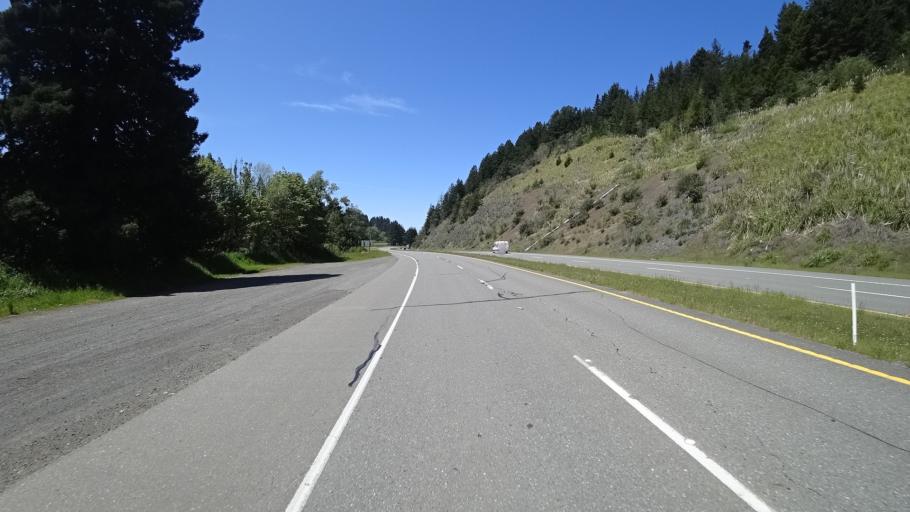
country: US
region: California
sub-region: Humboldt County
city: Arcata
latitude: 40.9096
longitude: -124.0505
